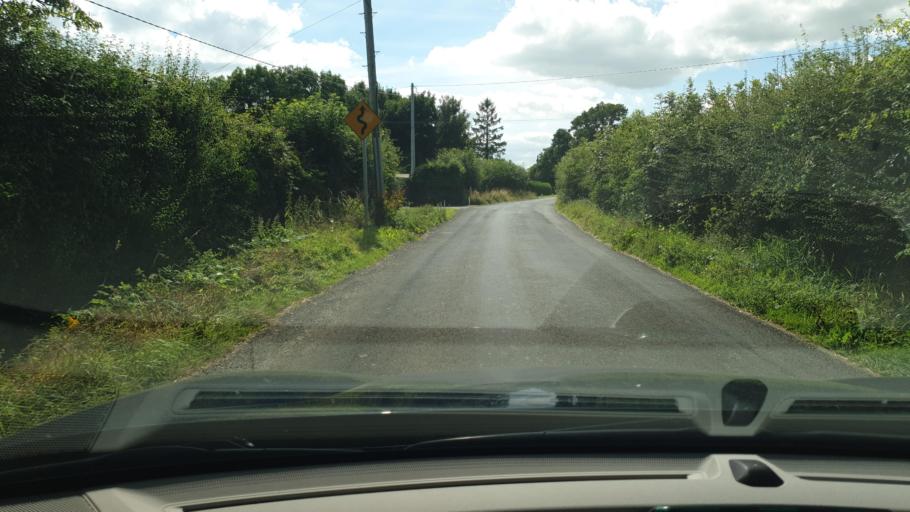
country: IE
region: Leinster
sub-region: An Mhi
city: Dunboyne
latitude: 53.4119
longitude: -6.4880
